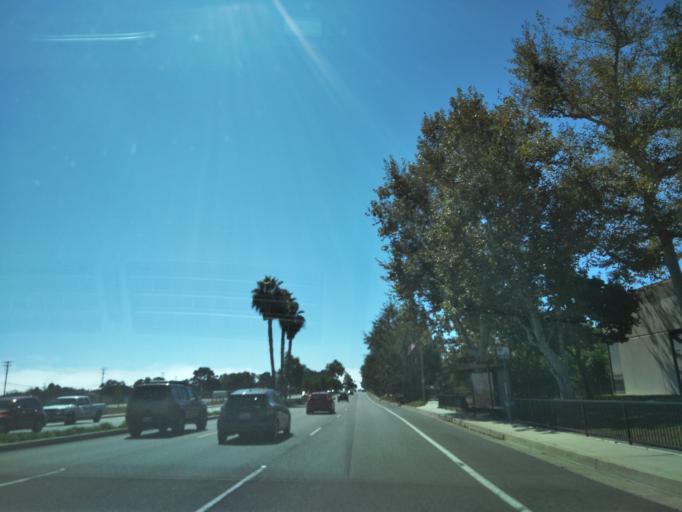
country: US
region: California
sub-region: Orange County
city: Seal Beach
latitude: 33.7526
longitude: -118.0875
